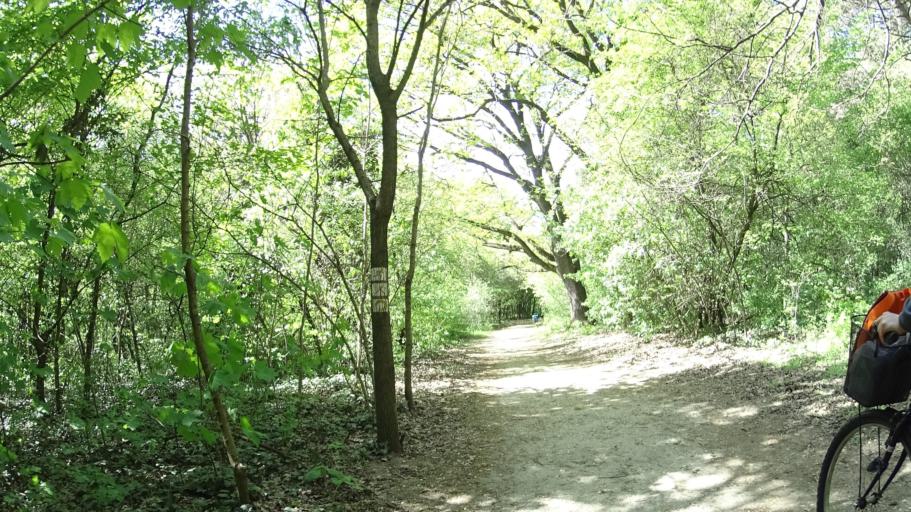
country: HU
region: Pest
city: Godollo
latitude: 47.5971
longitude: 19.3347
